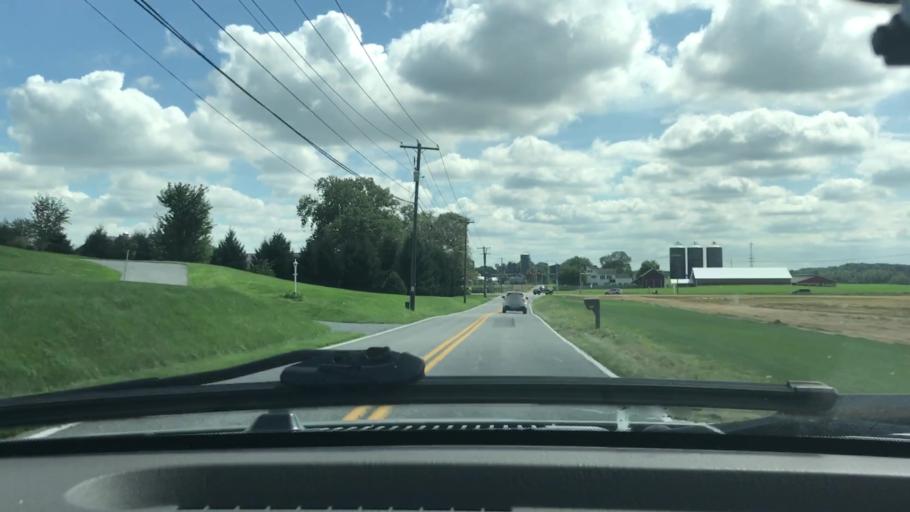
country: US
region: Pennsylvania
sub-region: Lancaster County
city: East Petersburg
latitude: 40.0958
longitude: -76.3794
